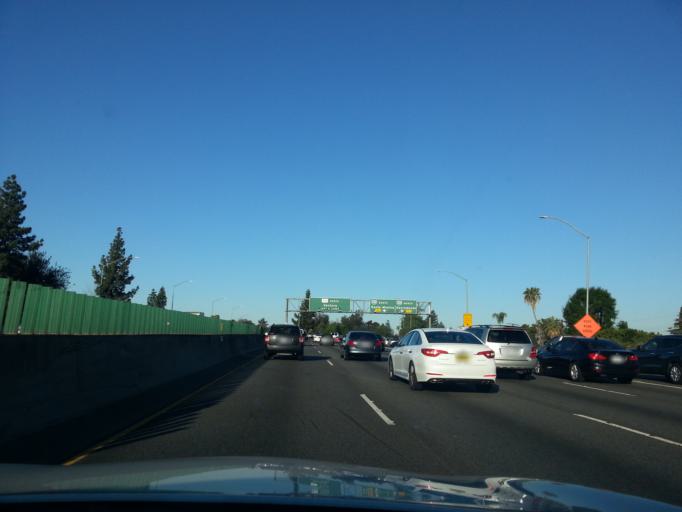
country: US
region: California
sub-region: Los Angeles County
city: Sherman Oaks
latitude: 34.1595
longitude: -118.4632
